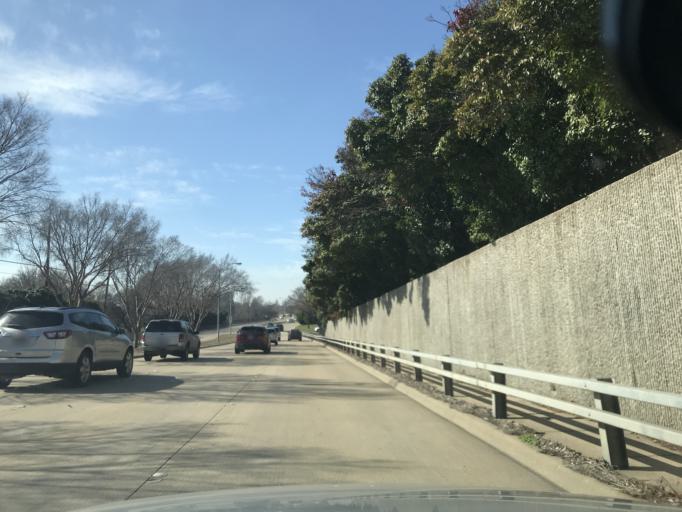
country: US
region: Texas
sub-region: Dallas County
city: Addison
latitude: 33.0425
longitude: -96.8049
